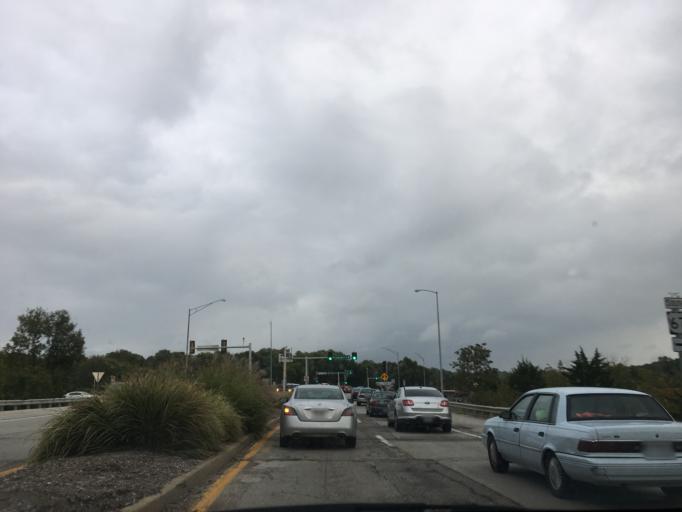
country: US
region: Missouri
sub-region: Saint Louis County
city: Maryland Heights
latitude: 38.7078
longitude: -90.4103
